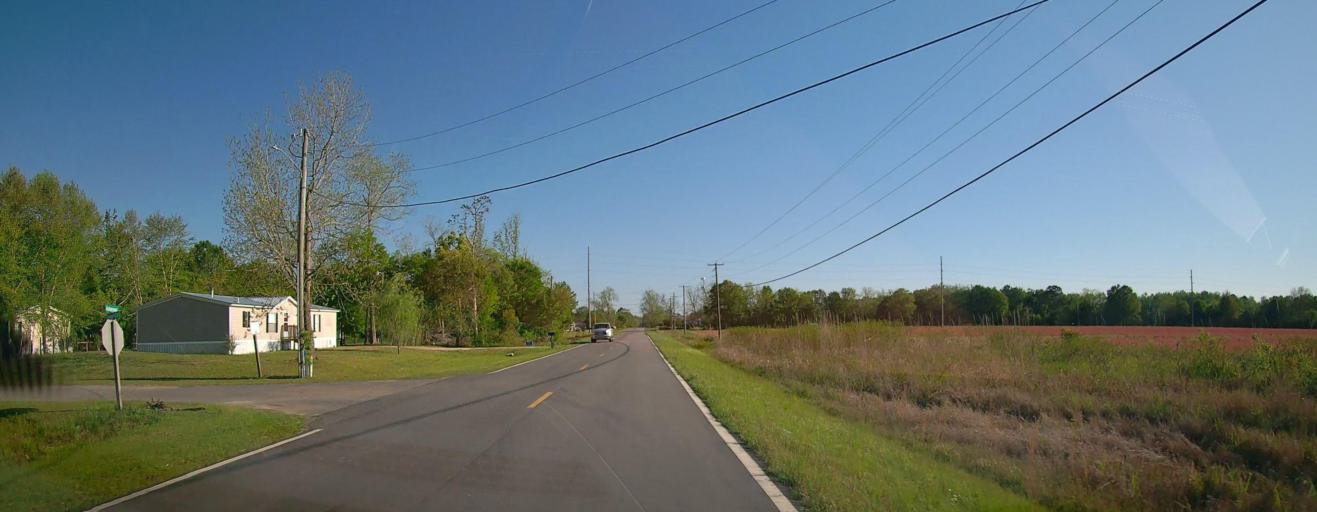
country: US
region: Georgia
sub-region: Ben Hill County
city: Fitzgerald
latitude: 31.7367
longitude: -83.2802
